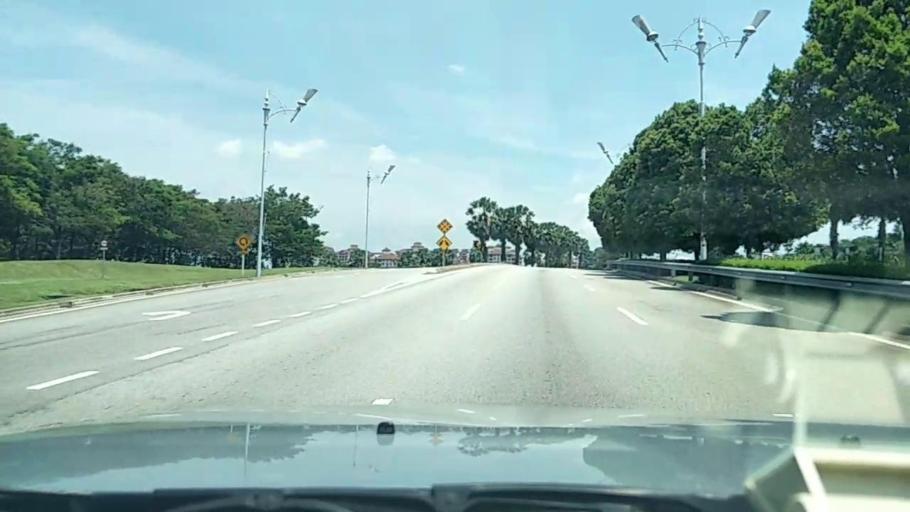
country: MY
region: Putrajaya
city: Putrajaya
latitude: 2.9516
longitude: 101.6835
